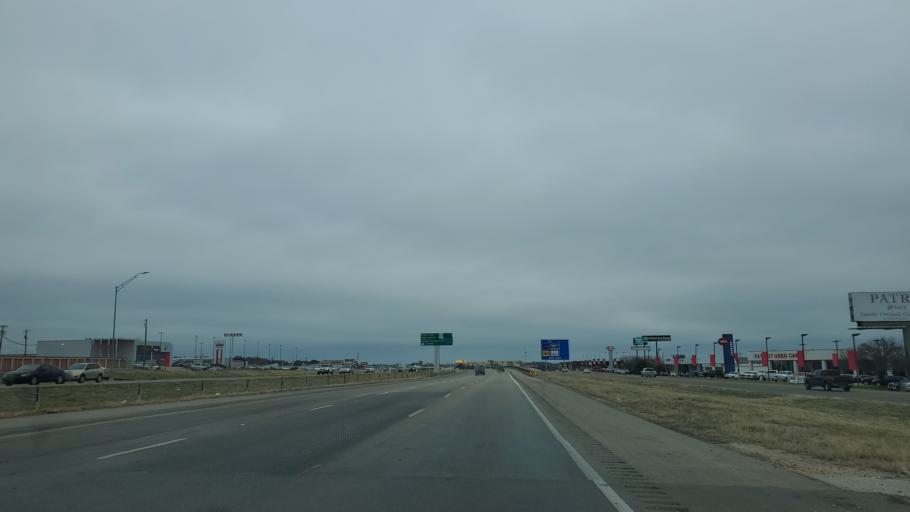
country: US
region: Texas
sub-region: Bell County
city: Harker Heights
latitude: 31.0786
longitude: -97.6952
